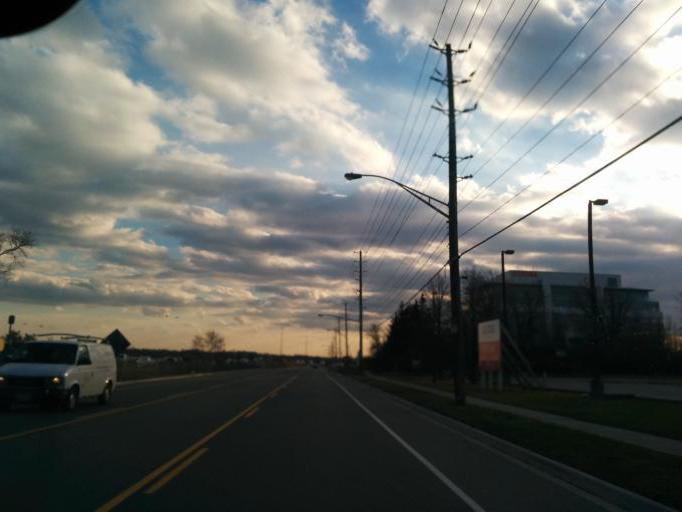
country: CA
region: Ontario
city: Oakville
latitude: 43.4817
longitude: -79.6732
